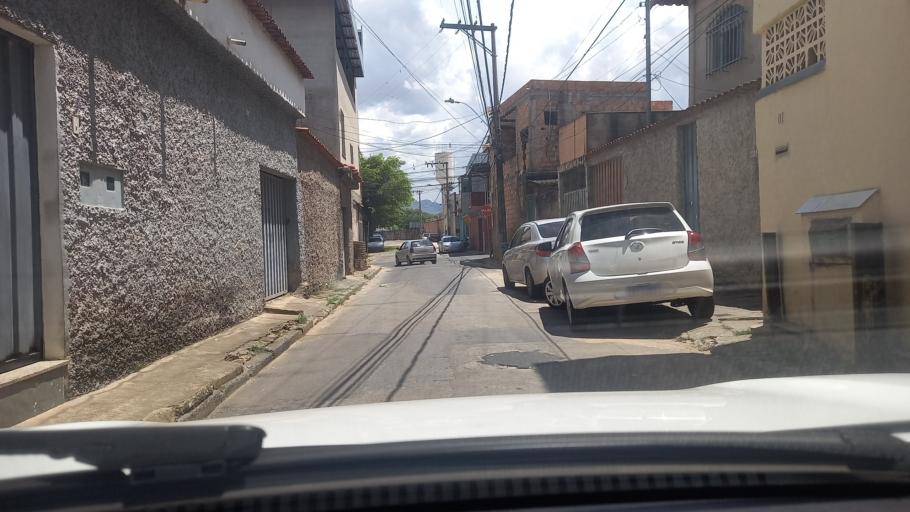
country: BR
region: Minas Gerais
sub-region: Belo Horizonte
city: Belo Horizonte
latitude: -19.9203
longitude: -43.9838
